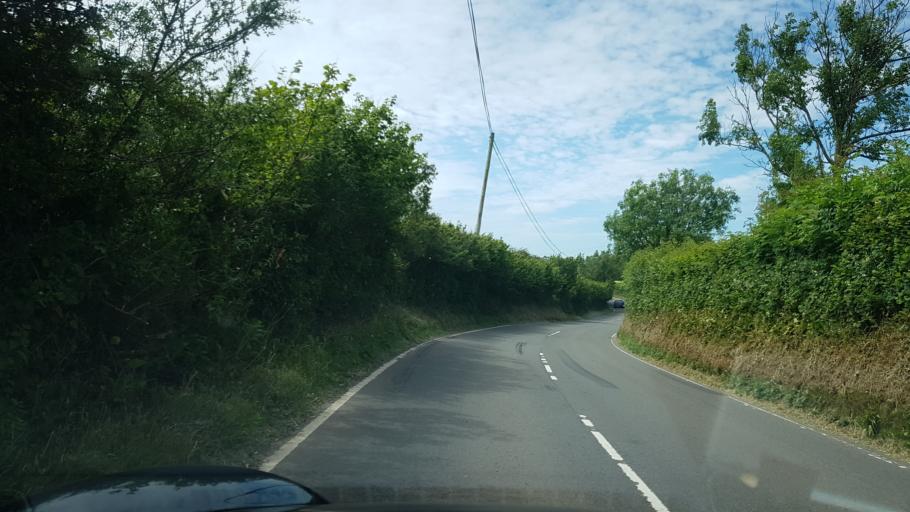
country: GB
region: Wales
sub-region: Carmarthenshire
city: Whitland
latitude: 51.7777
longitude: -4.6104
